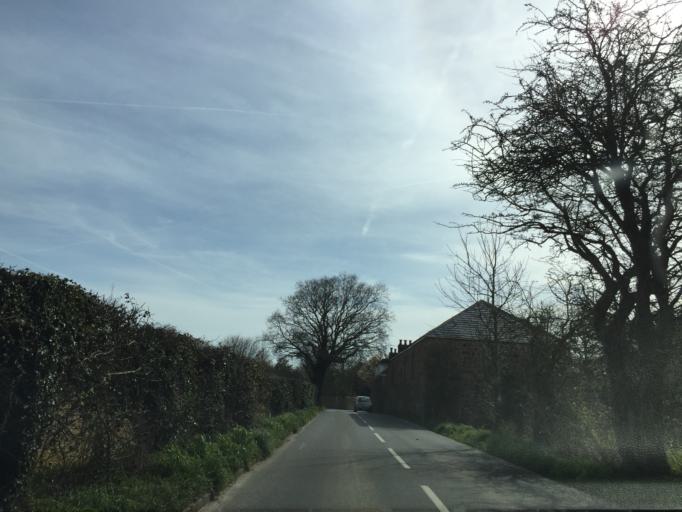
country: JE
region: St Helier
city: Saint Helier
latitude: 49.2208
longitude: -2.0593
